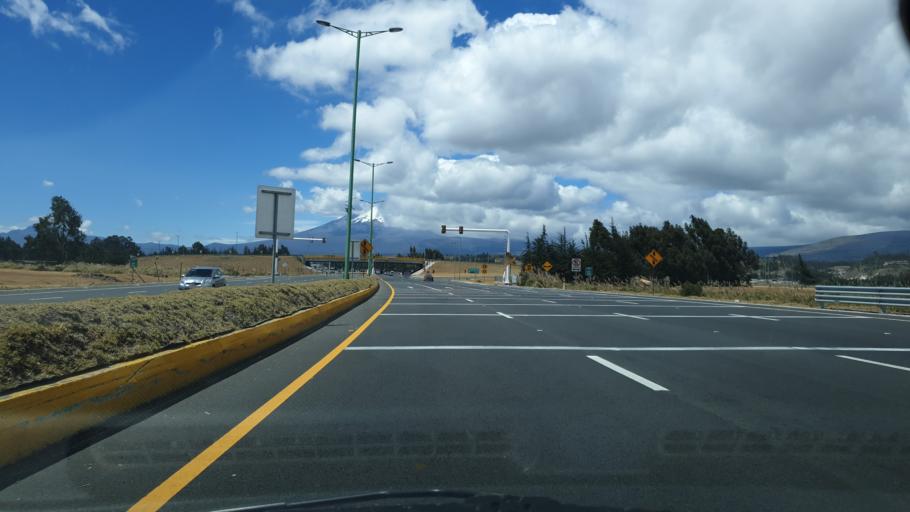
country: EC
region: Cotopaxi
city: Saquisili
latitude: -0.8674
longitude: -78.6293
